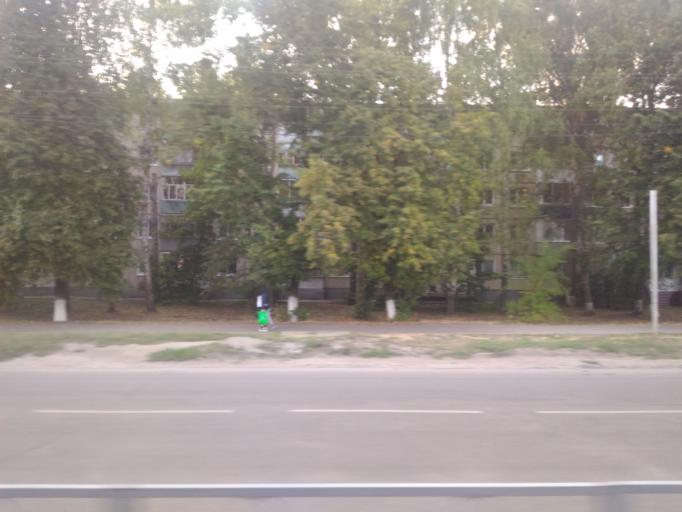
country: RU
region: Ulyanovsk
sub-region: Ulyanovskiy Rayon
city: Ulyanovsk
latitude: 54.2827
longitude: 48.2988
